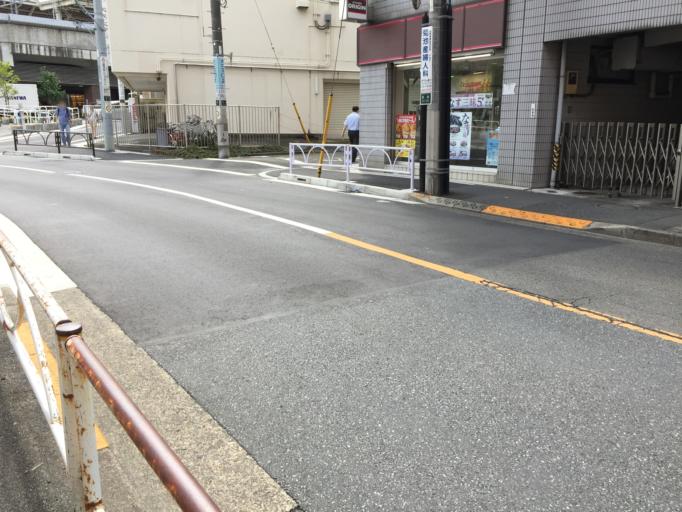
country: JP
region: Tokyo
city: Tokyo
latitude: 35.6526
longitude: 139.6380
